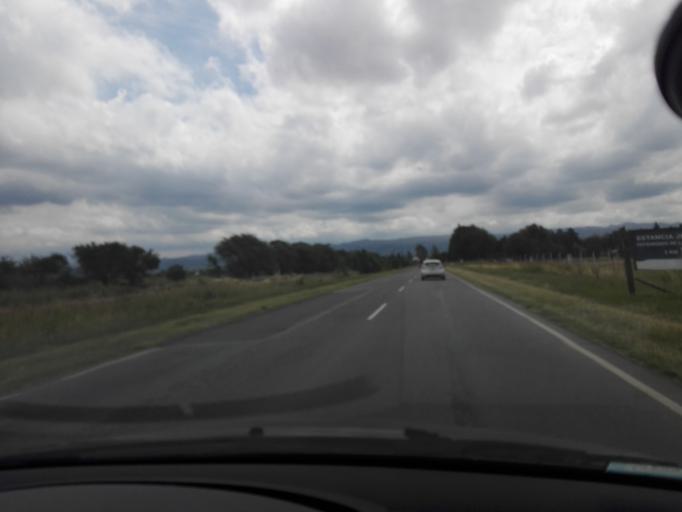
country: AR
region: Cordoba
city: Alta Gracia
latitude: -31.6582
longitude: -64.3950
